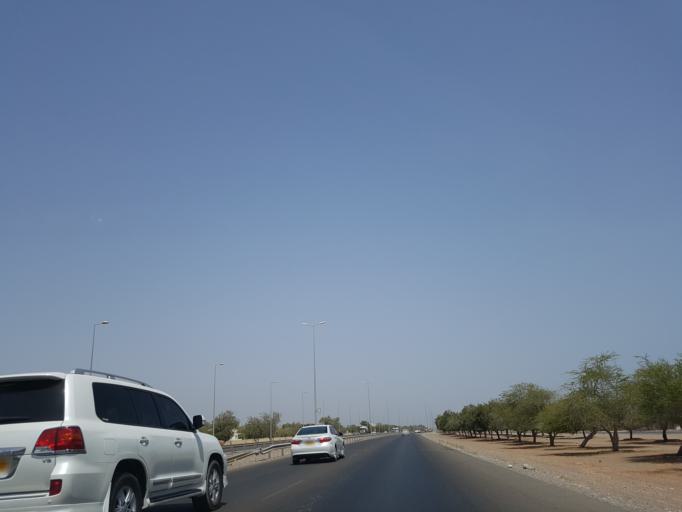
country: OM
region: Al Batinah
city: Saham
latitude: 24.0899
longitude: 56.9297
